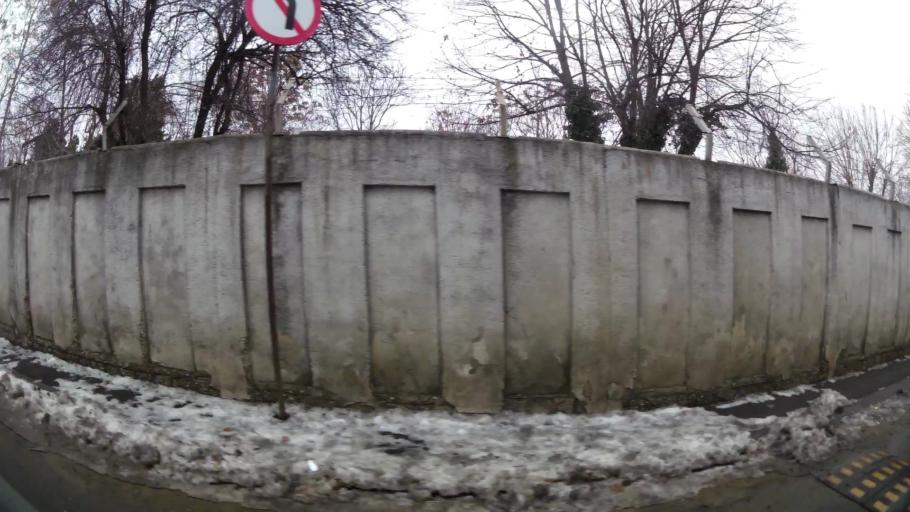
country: RO
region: Bucuresti
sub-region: Municipiul Bucuresti
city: Bucuresti
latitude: 44.4601
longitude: 26.0630
